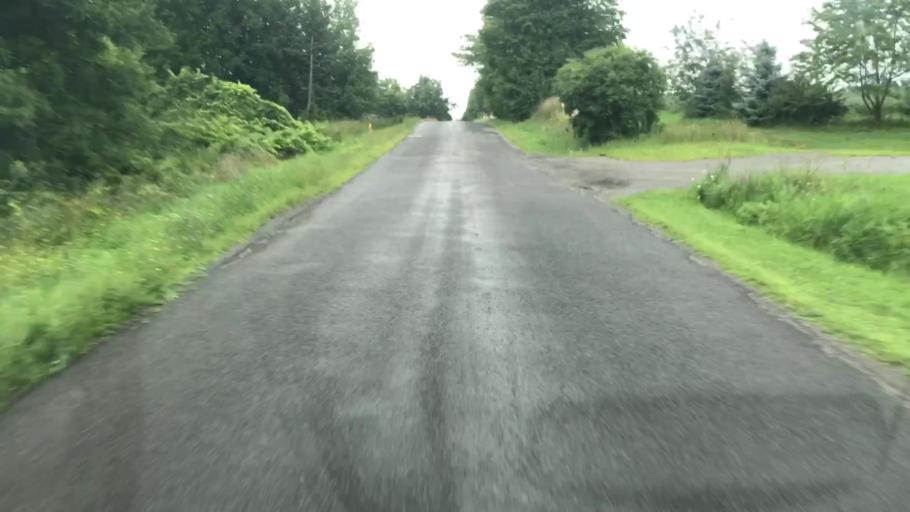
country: US
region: New York
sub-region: Cayuga County
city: Melrose Park
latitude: 42.9673
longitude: -76.5073
